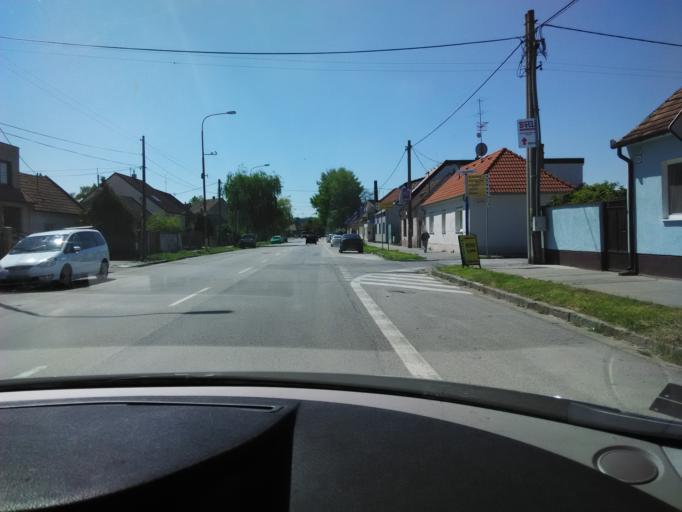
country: SK
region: Trnavsky
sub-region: Okres Trnava
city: Trnava
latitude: 48.3933
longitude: 17.5967
